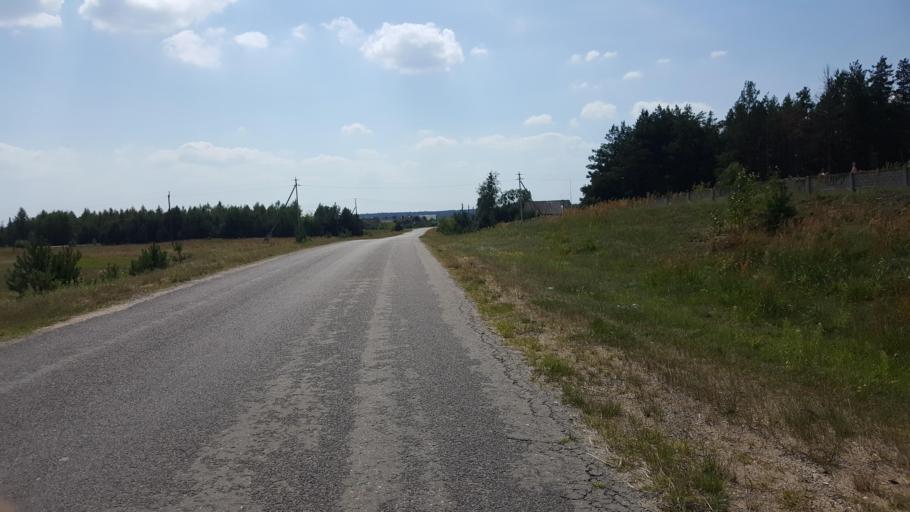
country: PL
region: Podlasie
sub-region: Powiat hajnowski
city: Czeremcha
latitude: 52.5422
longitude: 23.5440
